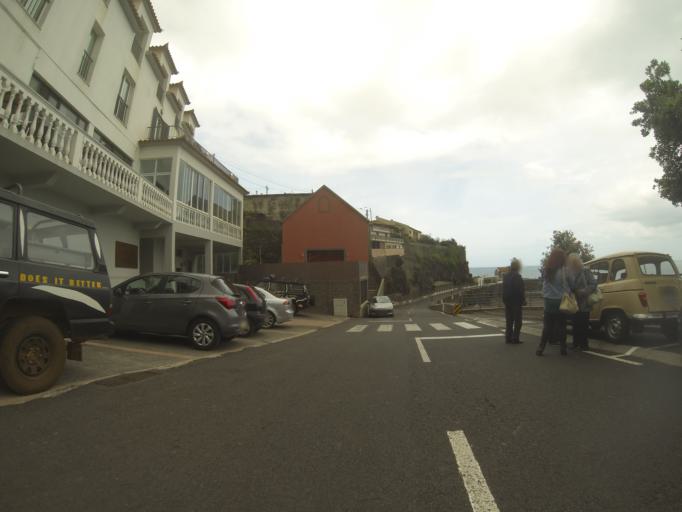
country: PT
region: Madeira
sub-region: Sao Vicente
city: Sao Vicente
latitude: 32.8216
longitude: -17.1035
